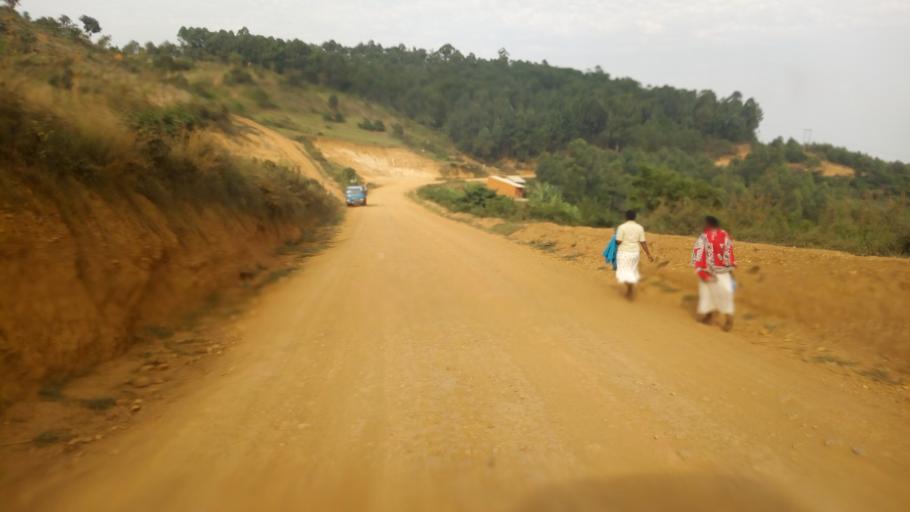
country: UG
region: Western Region
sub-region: Kanungu District
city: Ntungamo
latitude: -0.8307
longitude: 29.6972
